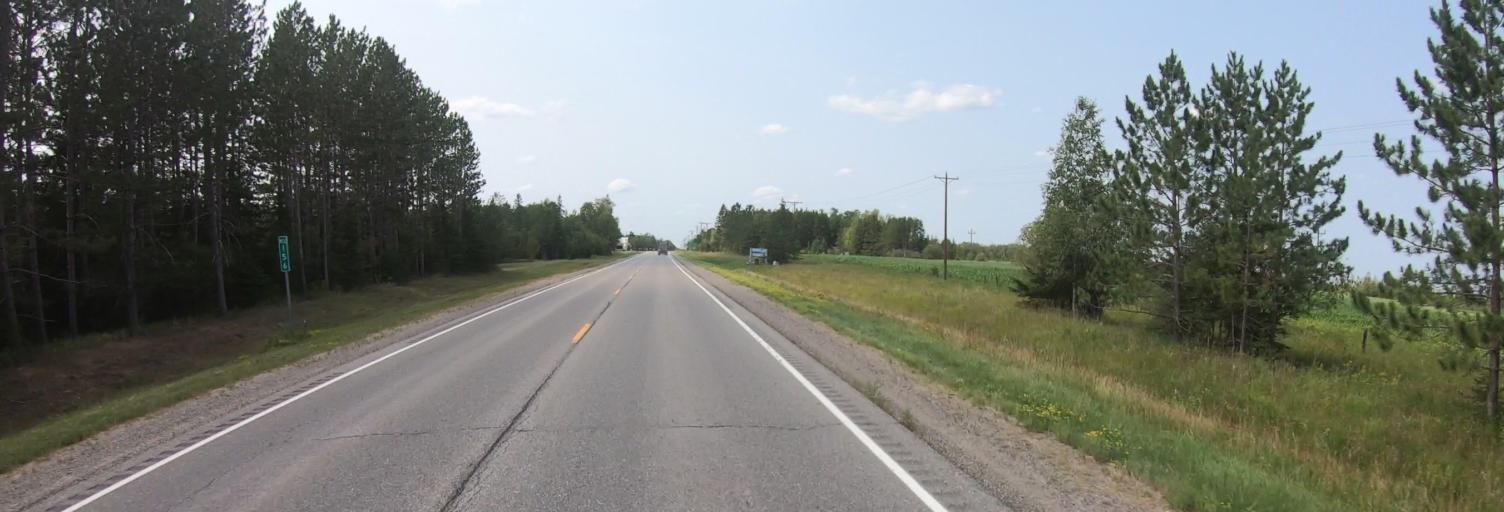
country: US
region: Minnesota
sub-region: Lake of the Woods County
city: Baudette
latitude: 48.6270
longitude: -94.0935
